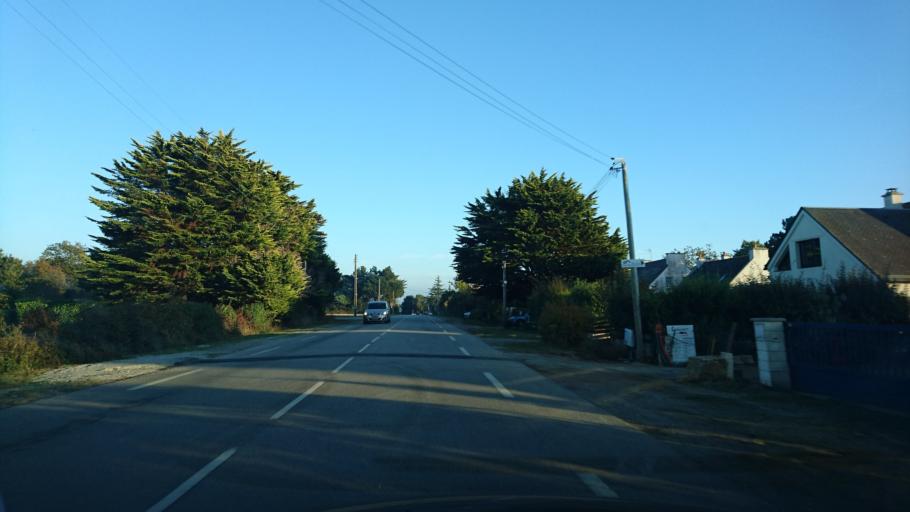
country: FR
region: Brittany
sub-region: Departement du Morbihan
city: Larmor-Baden
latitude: 47.6040
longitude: -2.8690
